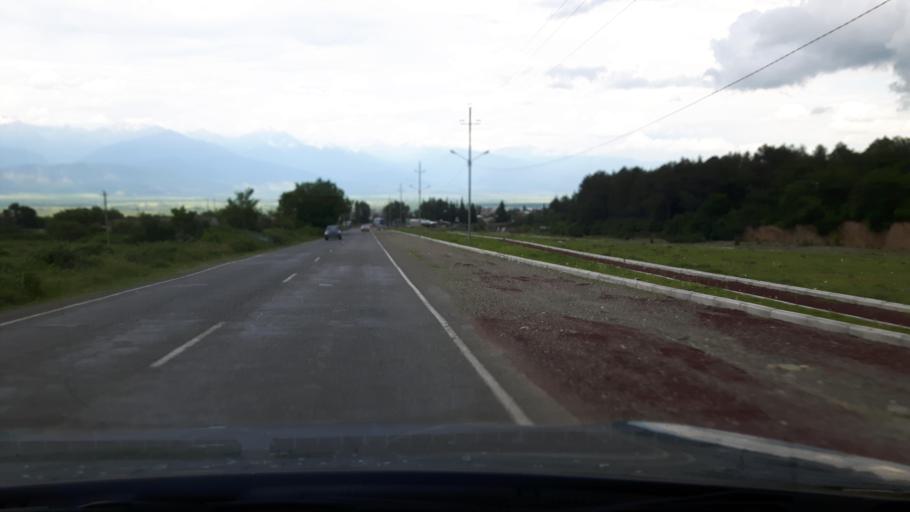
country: GE
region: Kakheti
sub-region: Telavi
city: Telavi
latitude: 41.9235
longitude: 45.4482
